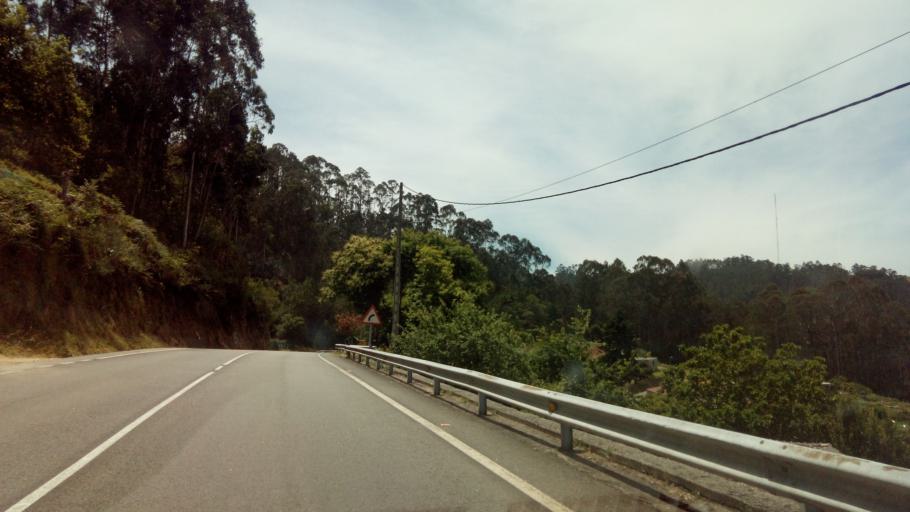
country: ES
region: Galicia
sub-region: Provincia de Pontevedra
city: Marin
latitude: 42.3457
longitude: -8.7060
